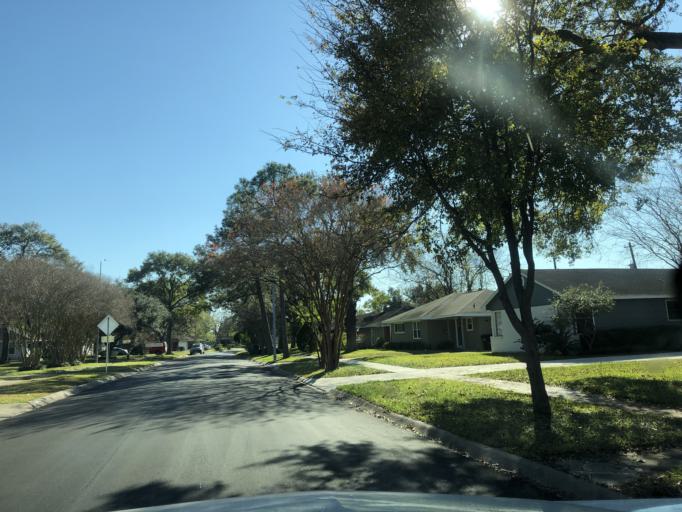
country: US
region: Texas
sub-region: Harris County
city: Bellaire
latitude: 29.6901
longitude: -95.5007
